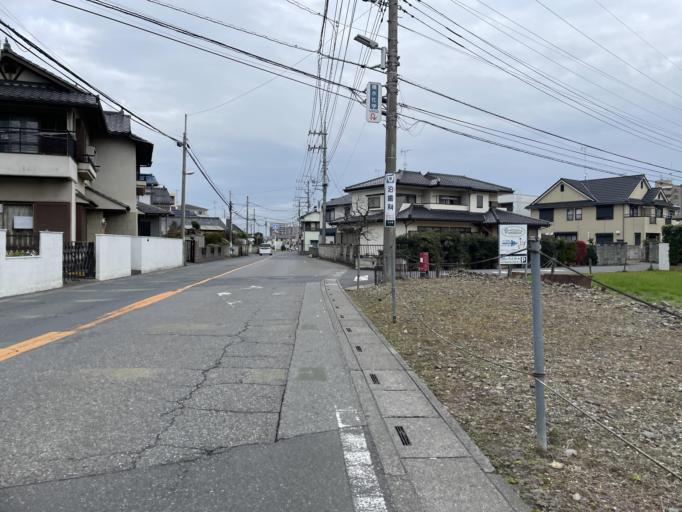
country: JP
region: Saitama
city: Shiraoka
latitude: 36.0123
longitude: 139.6607
